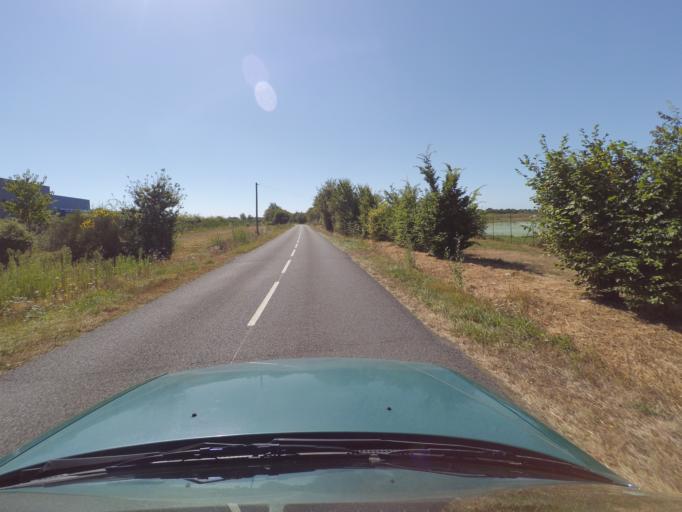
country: FR
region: Pays de la Loire
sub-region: Departement de la Loire-Atlantique
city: Le Bignon
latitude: 47.1181
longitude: -1.5045
